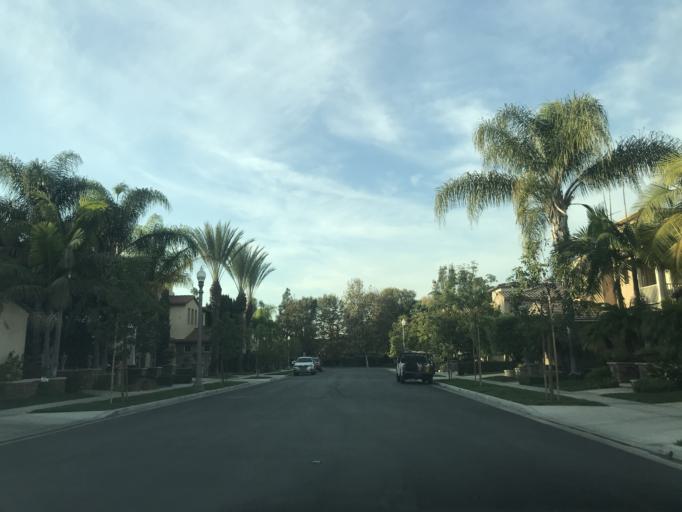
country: US
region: California
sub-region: Orange County
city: Irvine
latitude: 33.7017
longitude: -117.7604
